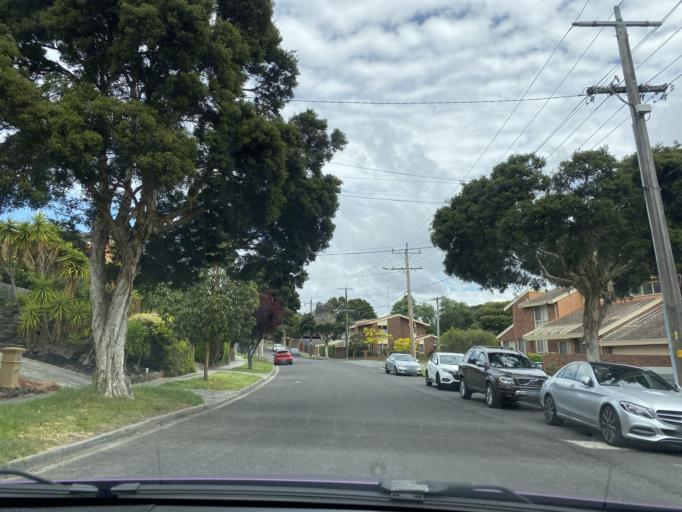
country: AU
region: Victoria
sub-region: Manningham
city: Templestowe Lower
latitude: -37.7681
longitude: 145.1265
